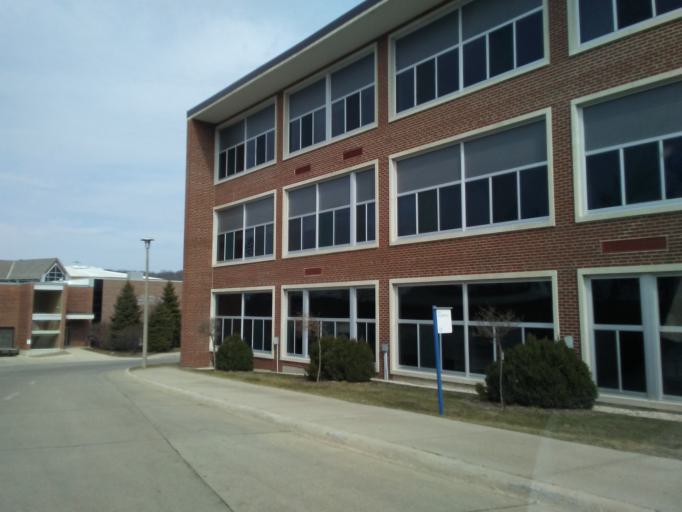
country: US
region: Iowa
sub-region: Winneshiek County
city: Decorah
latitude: 43.3112
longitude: -91.8065
